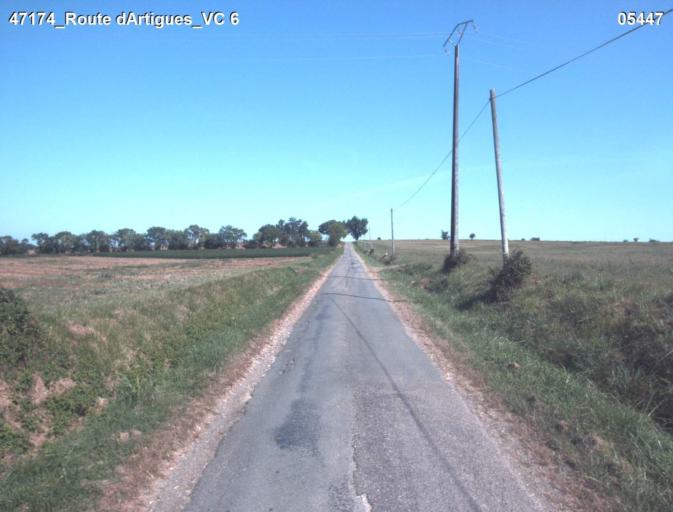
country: FR
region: Aquitaine
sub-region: Departement du Lot-et-Garonne
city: Mezin
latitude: 44.0477
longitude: 0.3330
